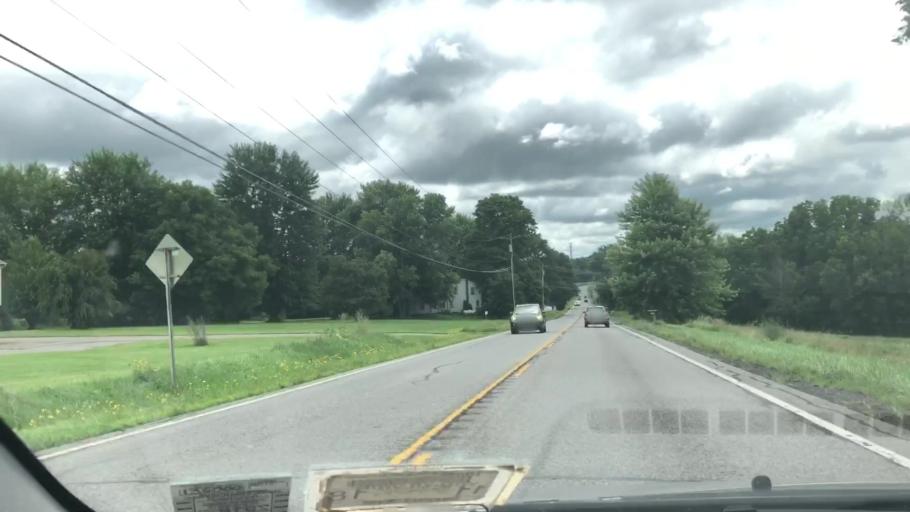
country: US
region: New York
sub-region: Wayne County
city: Macedon
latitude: 43.1062
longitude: -77.2929
